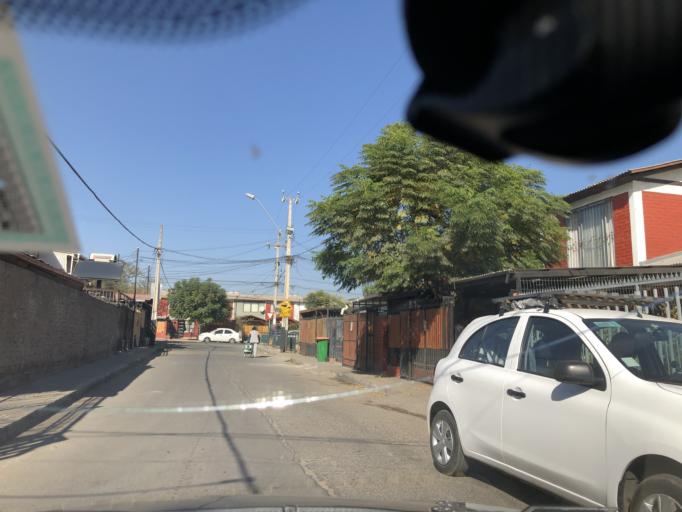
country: CL
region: Santiago Metropolitan
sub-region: Provincia de Cordillera
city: Puente Alto
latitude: -33.5815
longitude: -70.5885
